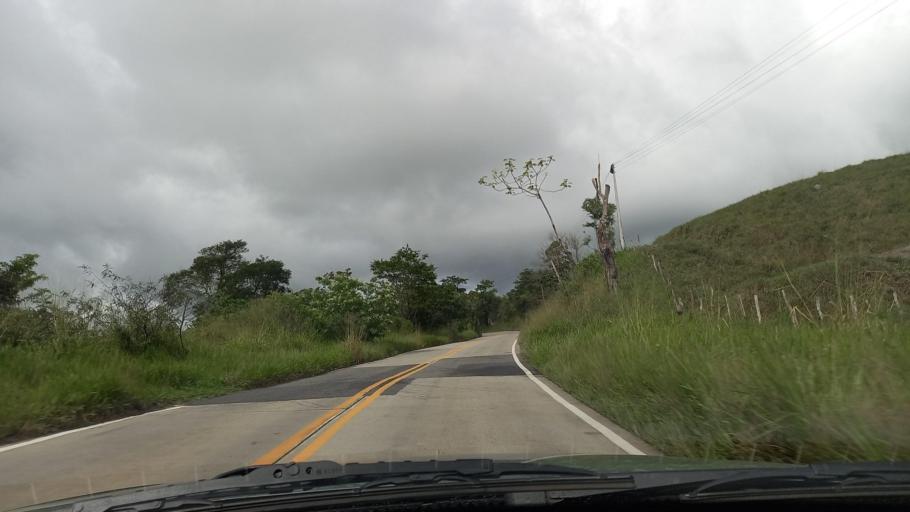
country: BR
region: Pernambuco
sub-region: Quipapa
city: Quipapa
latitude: -8.8048
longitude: -36.0083
